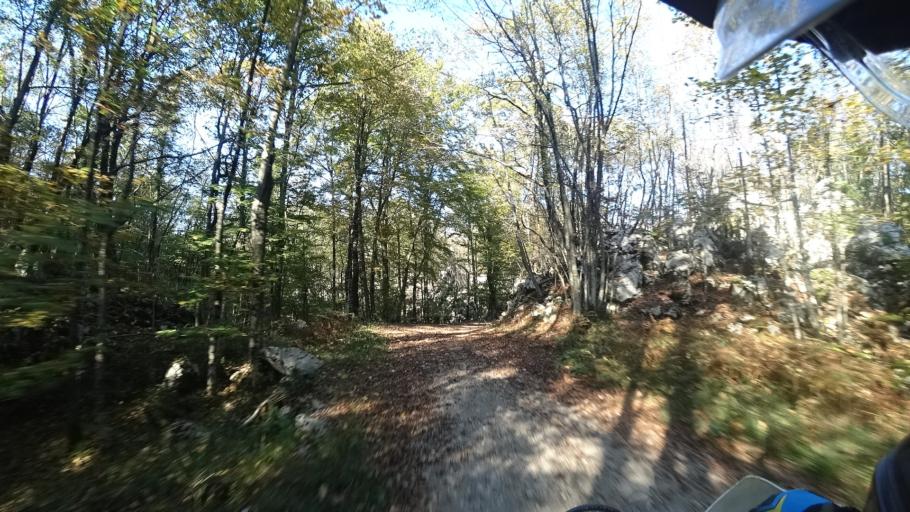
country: HR
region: Primorsko-Goranska
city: Kastav
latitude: 45.4081
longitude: 14.3370
